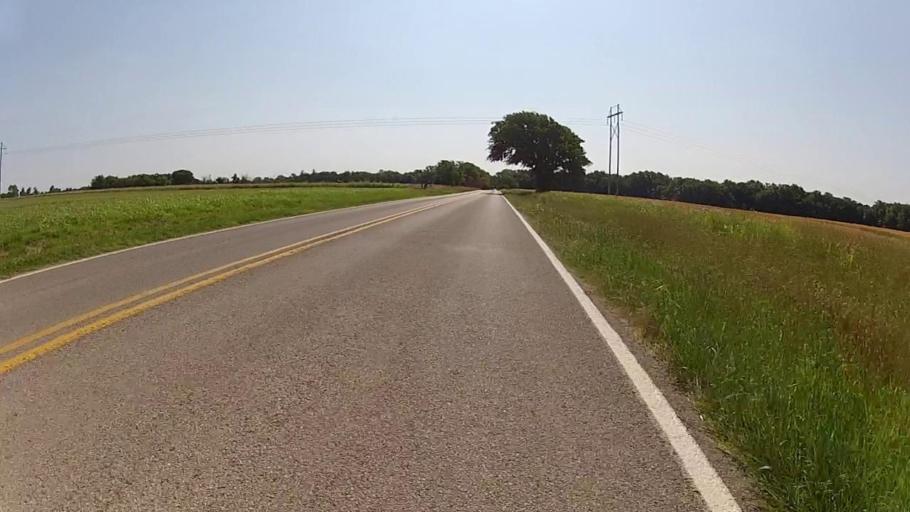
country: US
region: Kansas
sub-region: Montgomery County
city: Independence
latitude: 37.1930
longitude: -95.7388
